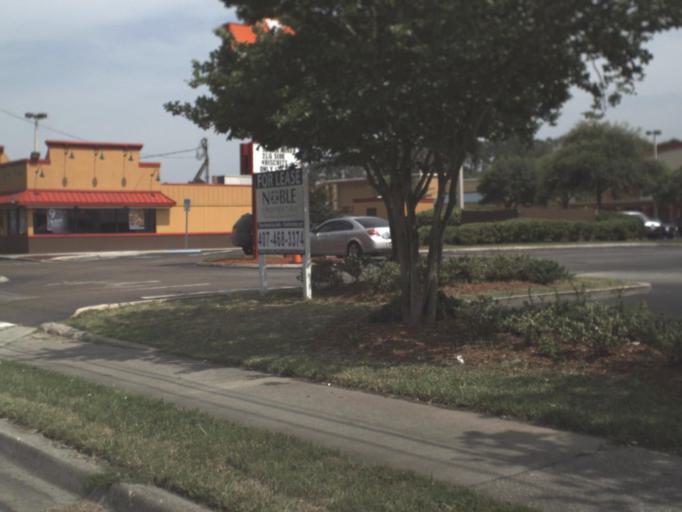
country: US
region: Florida
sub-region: Clay County
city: Bellair-Meadowbrook Terrace
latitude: 30.2483
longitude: -81.7462
